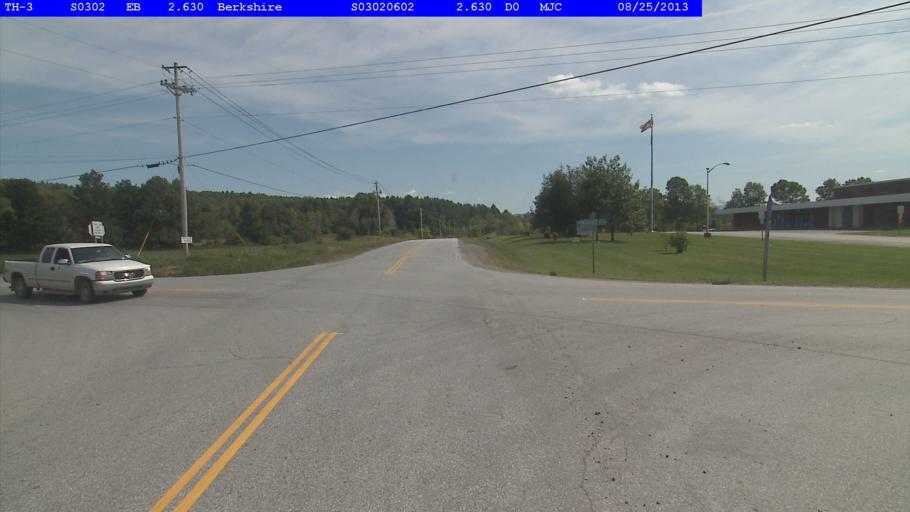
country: US
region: Vermont
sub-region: Franklin County
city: Enosburg Falls
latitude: 44.9733
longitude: -72.7663
